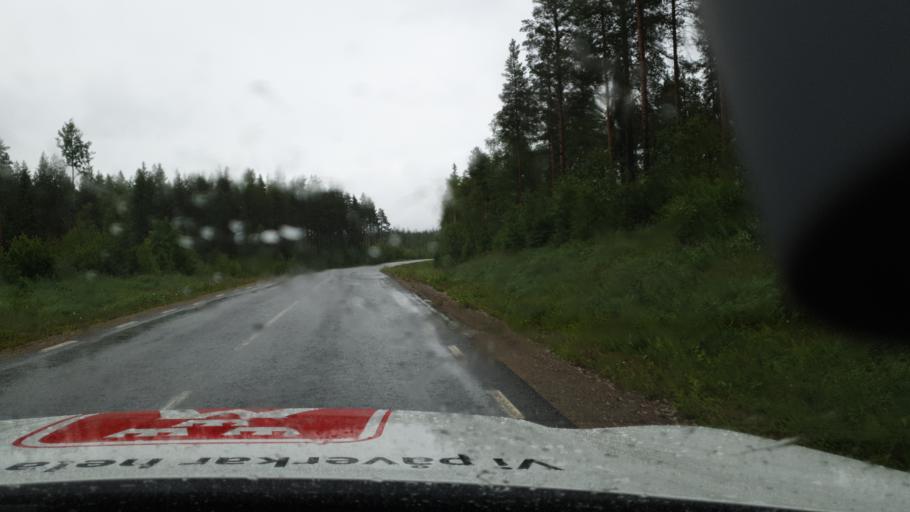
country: SE
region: Vaesterbotten
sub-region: Vindelns Kommun
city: Vindeln
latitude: 64.5528
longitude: 19.9175
